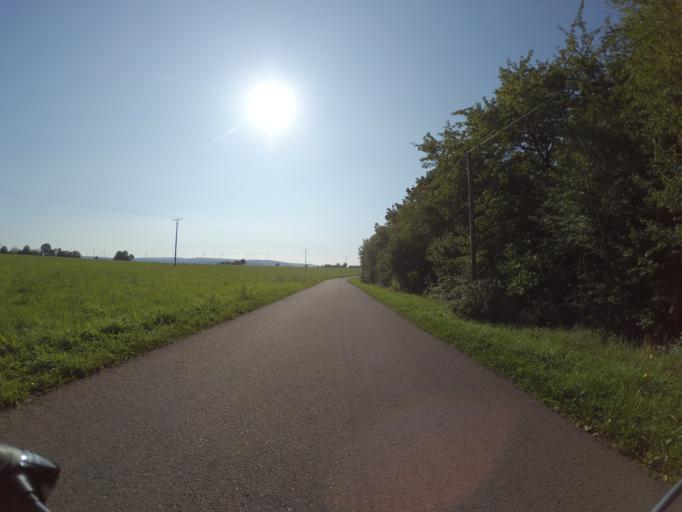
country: DE
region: Rheinland-Pfalz
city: Neumagen-Dhron
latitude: 49.8457
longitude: 6.9044
